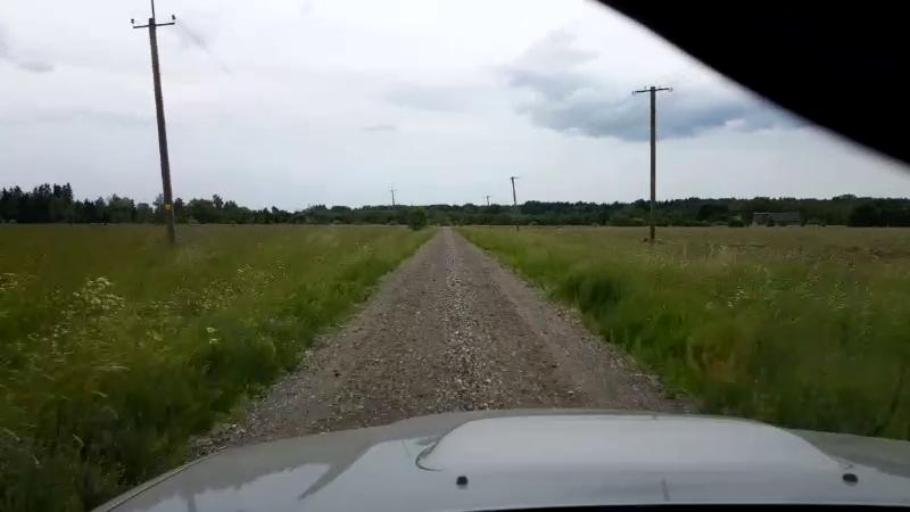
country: EE
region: Paernumaa
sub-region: Halinga vald
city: Parnu-Jaagupi
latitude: 58.5283
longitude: 24.6131
